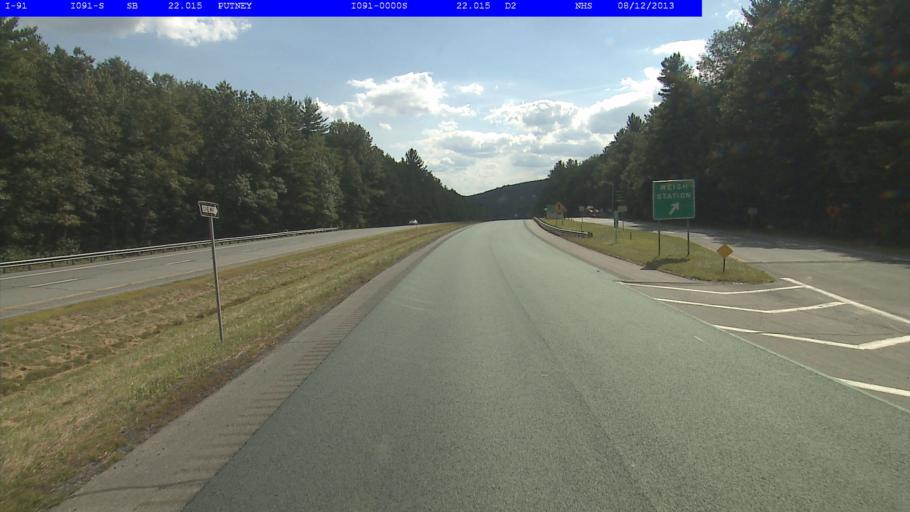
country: US
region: New Hampshire
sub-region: Cheshire County
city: Westmoreland
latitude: 42.9990
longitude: -72.4699
